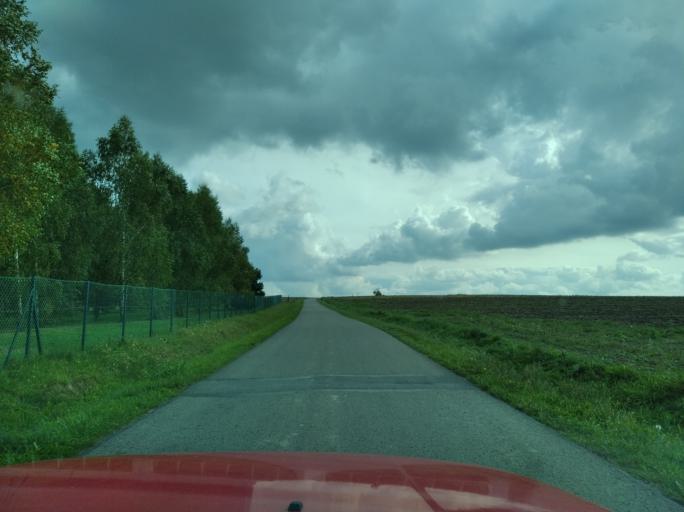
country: PL
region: Subcarpathian Voivodeship
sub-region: Powiat rzeszowski
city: Lubenia
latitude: 49.9383
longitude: 21.9402
